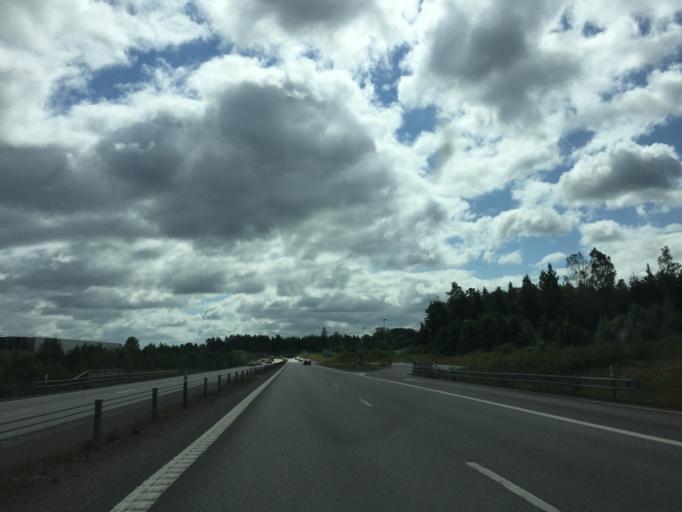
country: SE
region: OErebro
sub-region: Orebro Kommun
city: Orebro
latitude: 59.2419
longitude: 15.1015
